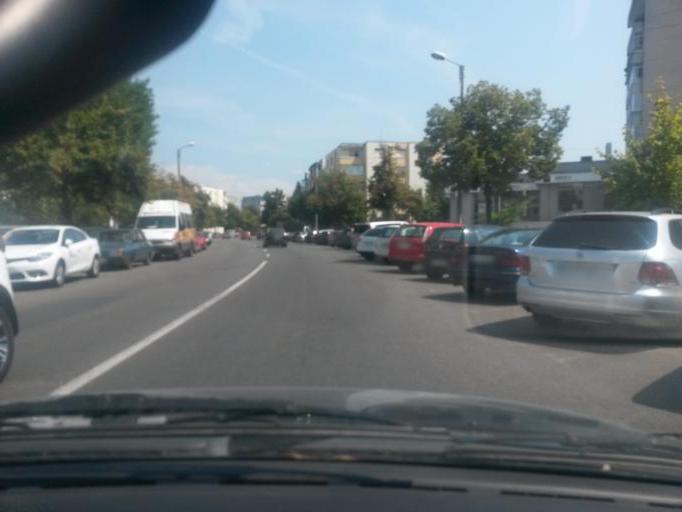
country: RO
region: Mures
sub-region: Comuna Corunca
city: Corunca
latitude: 46.5365
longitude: 24.5922
